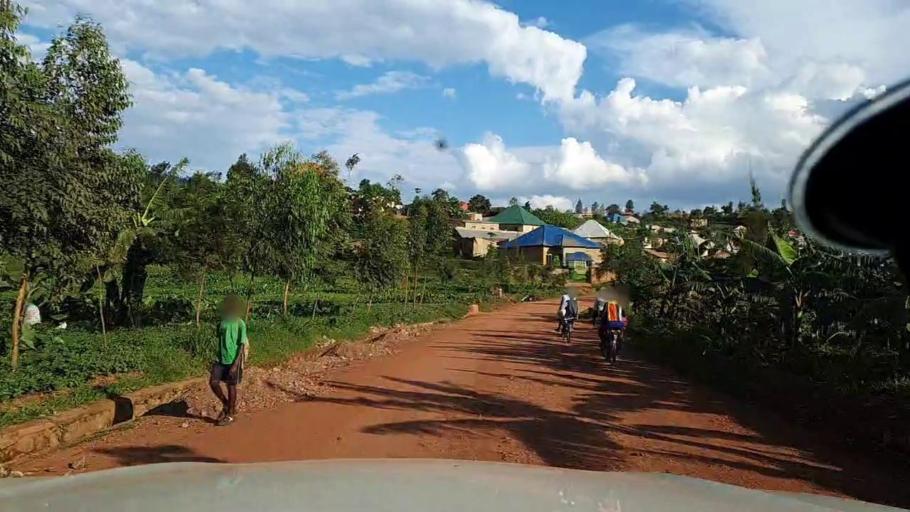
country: RW
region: Kigali
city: Kigali
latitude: -1.8946
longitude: 29.9641
